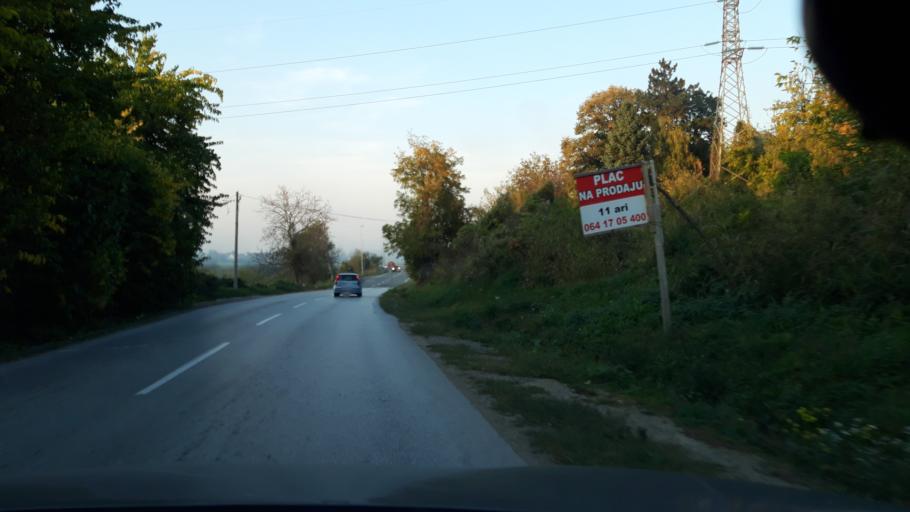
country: RS
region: Autonomna Pokrajina Vojvodina
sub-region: Juznobacki Okrug
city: Novi Sad
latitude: 45.2082
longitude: 19.8408
